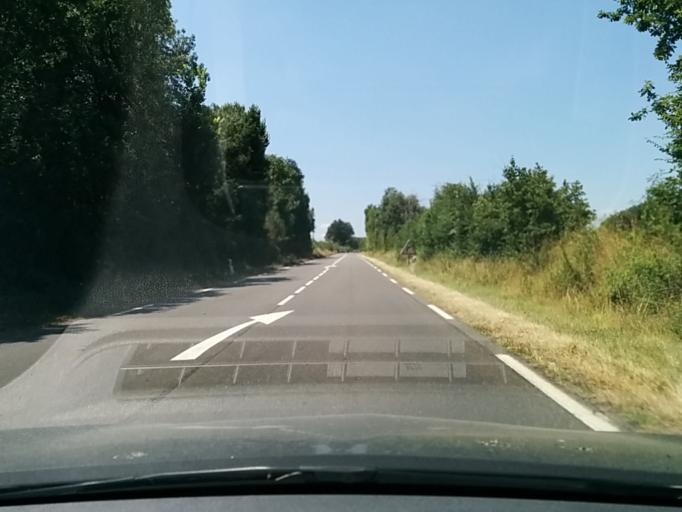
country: FR
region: Midi-Pyrenees
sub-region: Departement du Gers
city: Gimont
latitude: 43.6177
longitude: 0.9200
